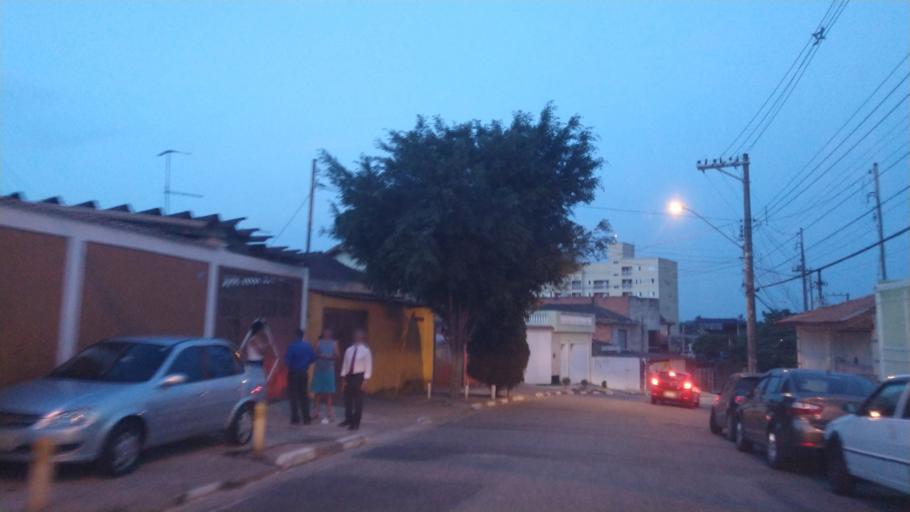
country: BR
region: Sao Paulo
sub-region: Aruja
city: Aruja
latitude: -23.4104
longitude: -46.4028
